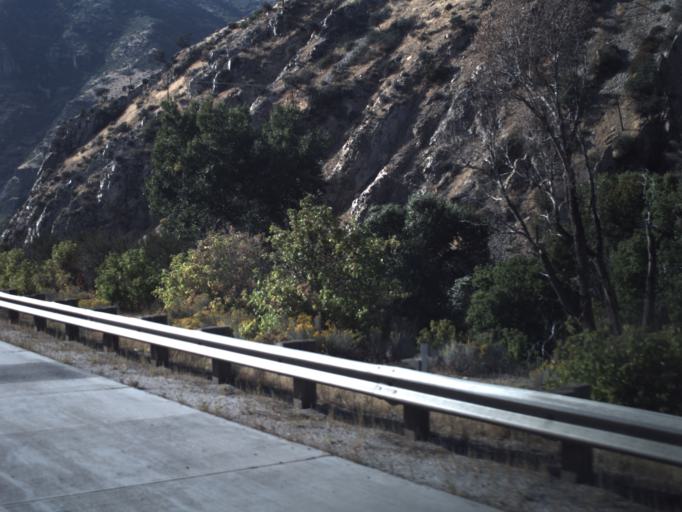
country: US
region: Utah
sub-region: Morgan County
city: Morgan
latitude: 41.0586
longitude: -111.5833
